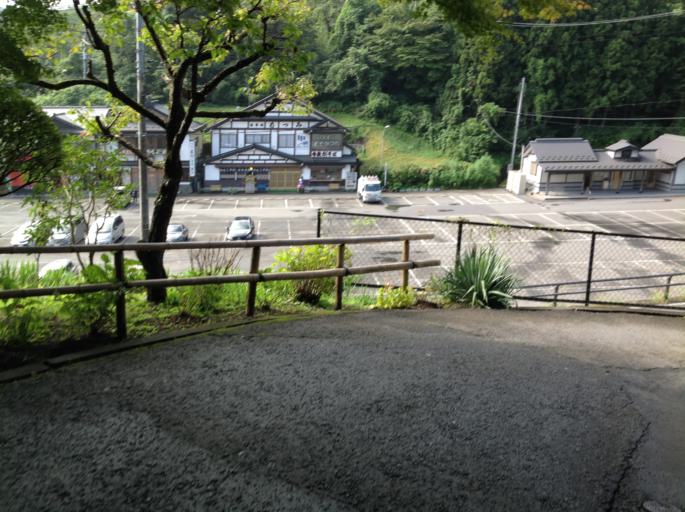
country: JP
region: Iwate
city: Ichinoseki
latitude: 38.9984
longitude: 141.1073
